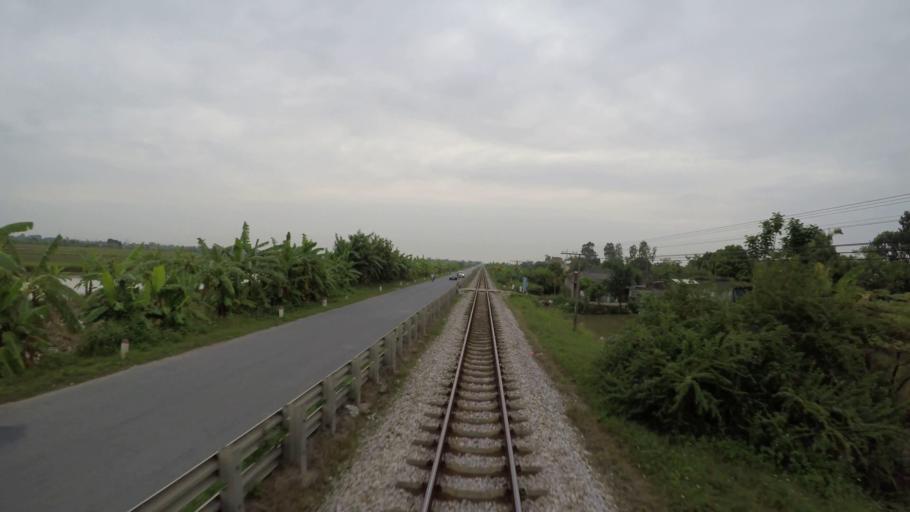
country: VN
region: Hung Yen
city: Ban Yen Nhan
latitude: 20.9797
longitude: 106.0817
